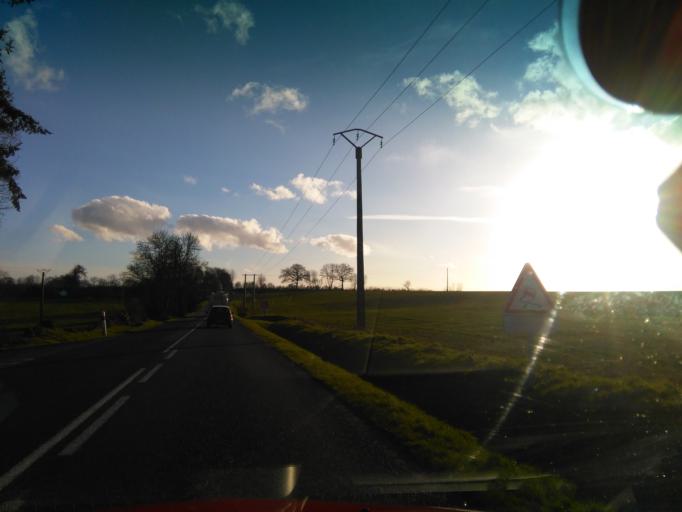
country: FR
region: Lower Normandy
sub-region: Departement de l'Orne
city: Pont-Ecrepin
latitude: 48.7123
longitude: -0.2749
